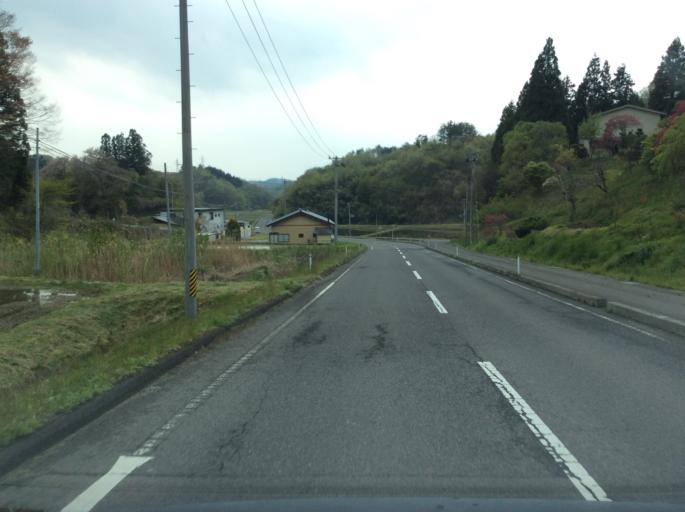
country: JP
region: Fukushima
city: Miharu
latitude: 37.3996
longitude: 140.5249
